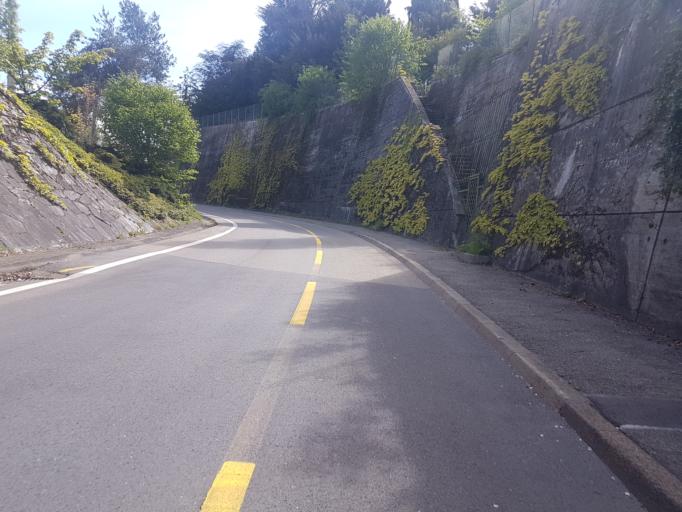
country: CH
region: Geneva
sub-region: Geneva
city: Bellevue
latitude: 46.2455
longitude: 6.1511
